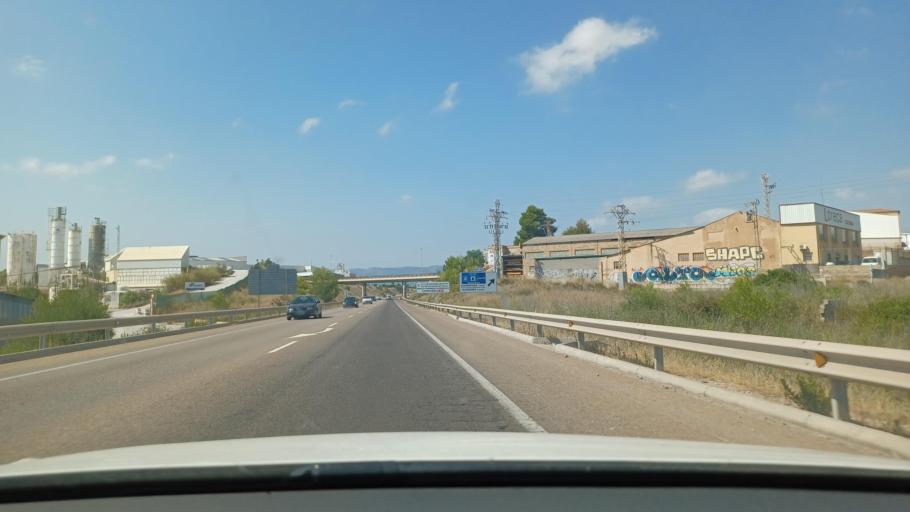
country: ES
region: Valencia
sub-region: Provincia de Castello
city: Vila-real
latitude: 39.9559
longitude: -0.0856
